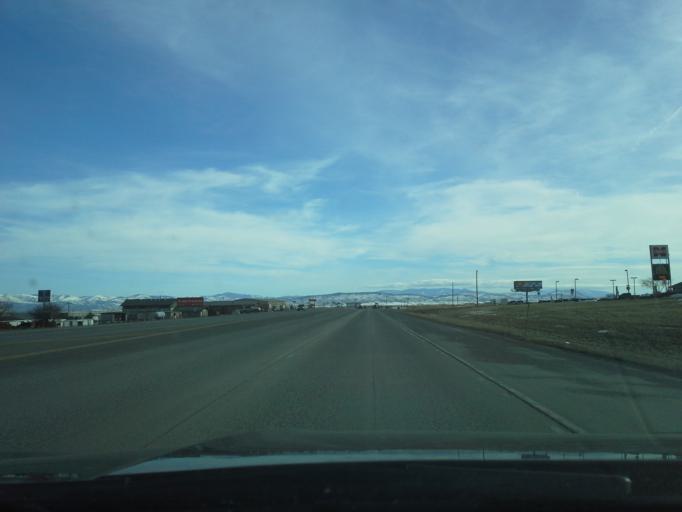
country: US
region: Montana
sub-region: Lewis and Clark County
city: Helena Valley Southeast
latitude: 46.5915
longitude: -111.9655
